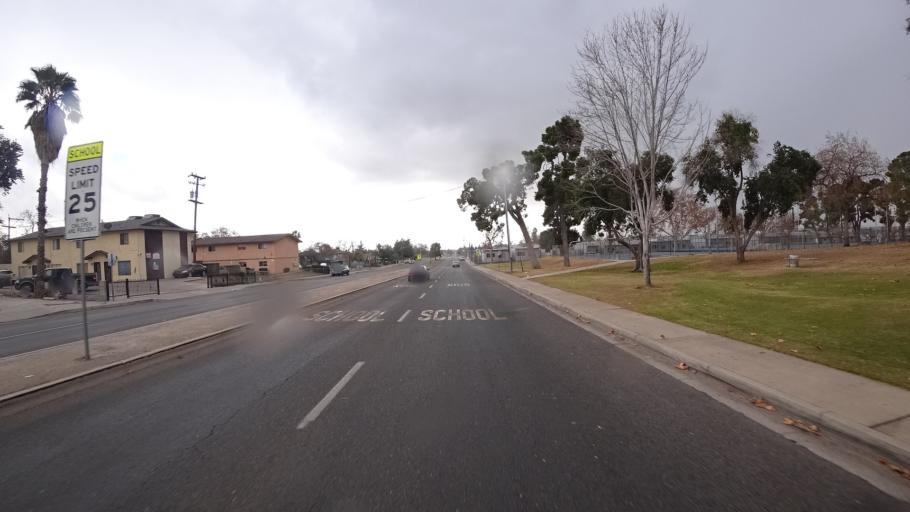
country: US
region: California
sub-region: Kern County
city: Bakersfield
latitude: 35.3885
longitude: -118.9854
